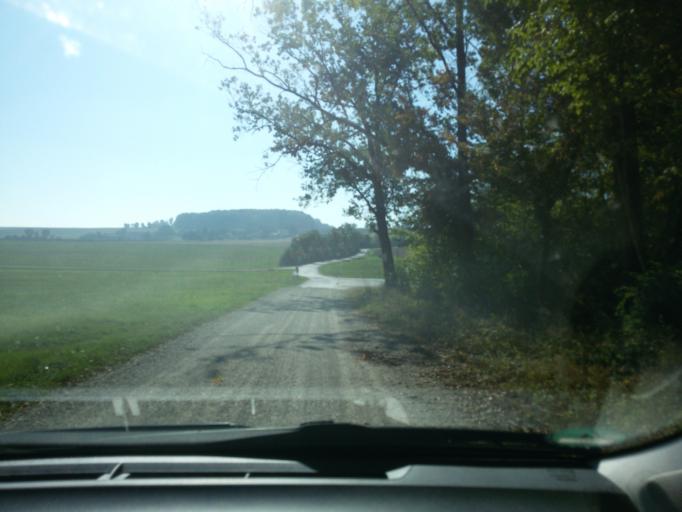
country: DE
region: Bavaria
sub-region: Swabia
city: Hainsfarth
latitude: 48.9859
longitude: 10.5847
